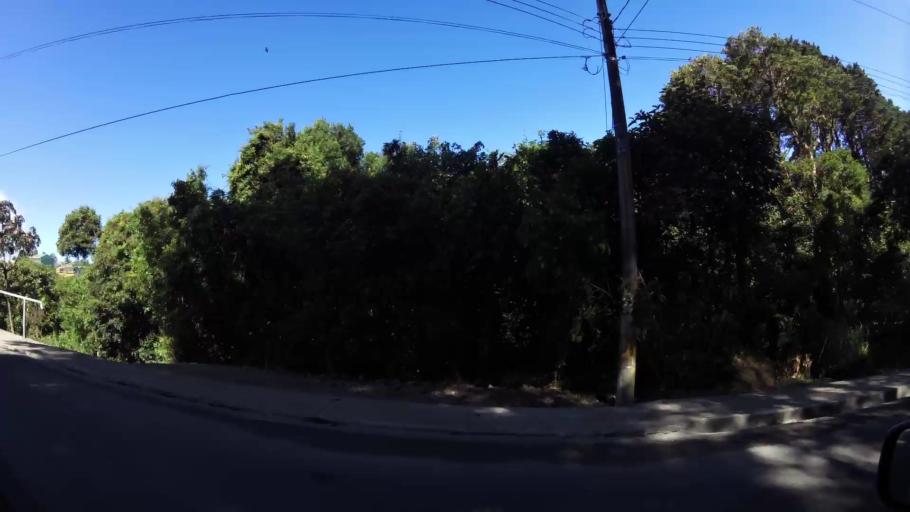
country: CR
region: Guanacaste
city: Juntas
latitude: 10.3160
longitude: -84.8244
